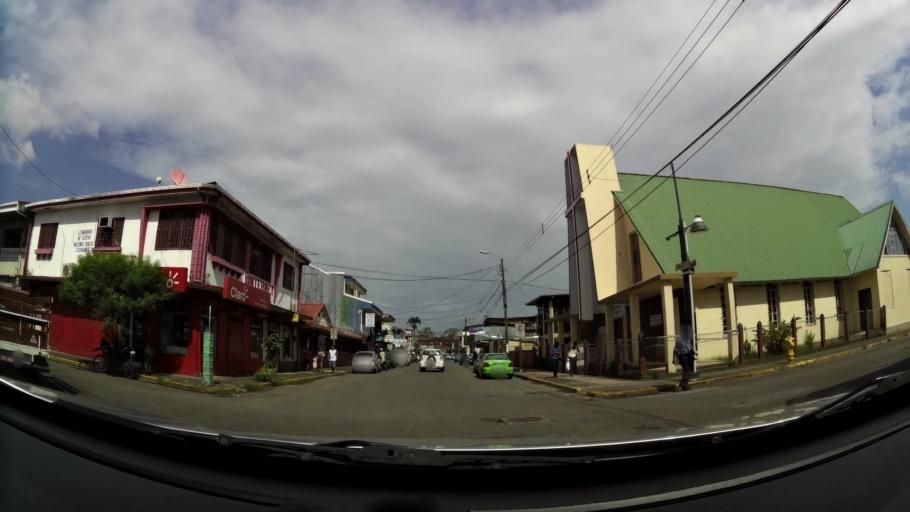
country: CR
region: Limon
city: Limon
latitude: 9.9942
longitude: -83.0285
